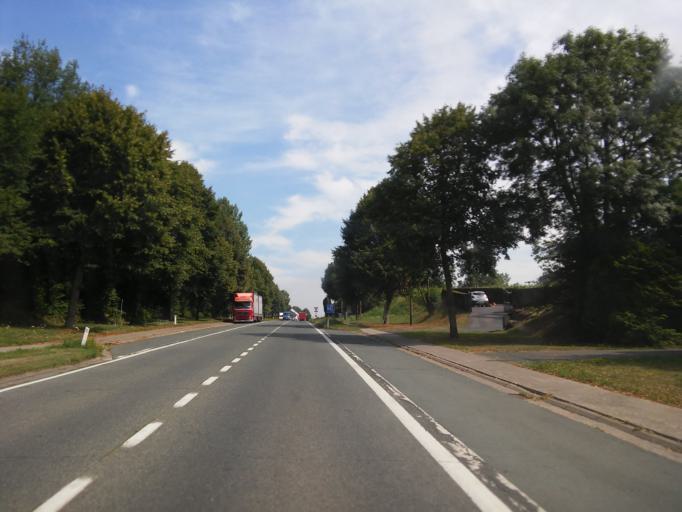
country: BE
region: Flanders
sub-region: Provincie Vlaams-Brabant
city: Gooik
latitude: 50.7933
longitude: 4.1257
